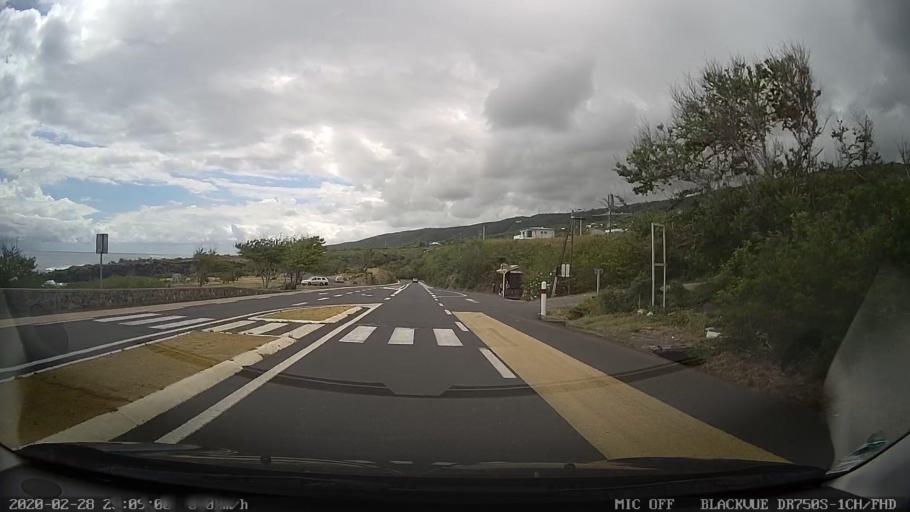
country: RE
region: Reunion
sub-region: Reunion
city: Trois-Bassins
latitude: -21.1294
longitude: 55.2697
